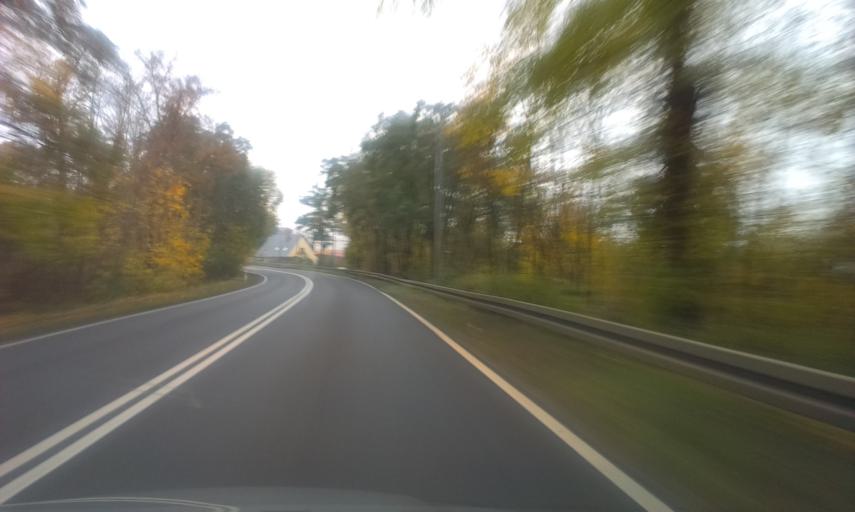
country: PL
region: Greater Poland Voivodeship
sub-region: Powiat chodzieski
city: Chodziez
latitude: 52.9876
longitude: 16.9043
